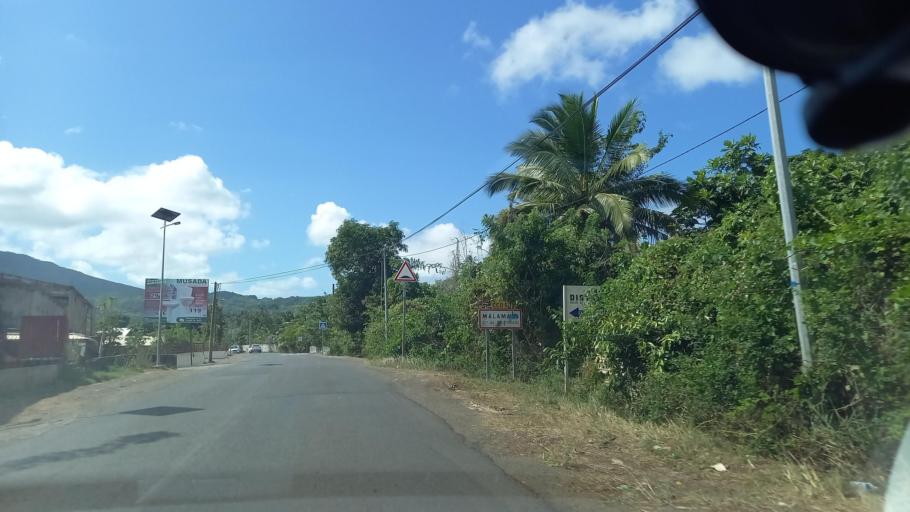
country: YT
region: Chirongui
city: Chirongui
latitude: -12.9236
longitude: 45.1566
